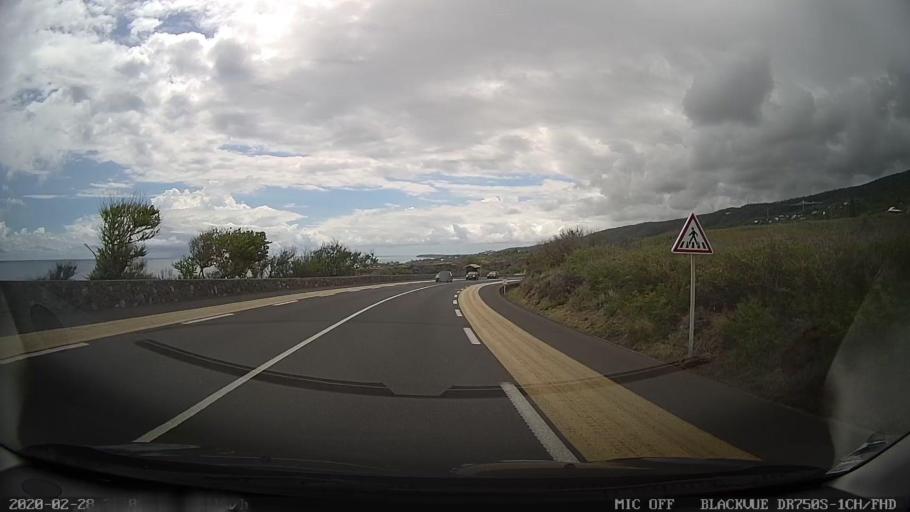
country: RE
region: Reunion
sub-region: Reunion
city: Trois-Bassins
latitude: -21.1305
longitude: 55.2704
